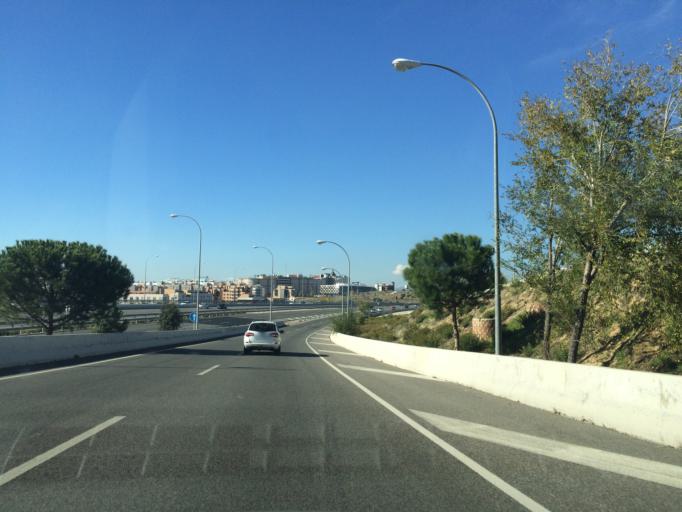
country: ES
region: Madrid
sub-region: Provincia de Madrid
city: Las Tablas
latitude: 40.5104
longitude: -3.6620
